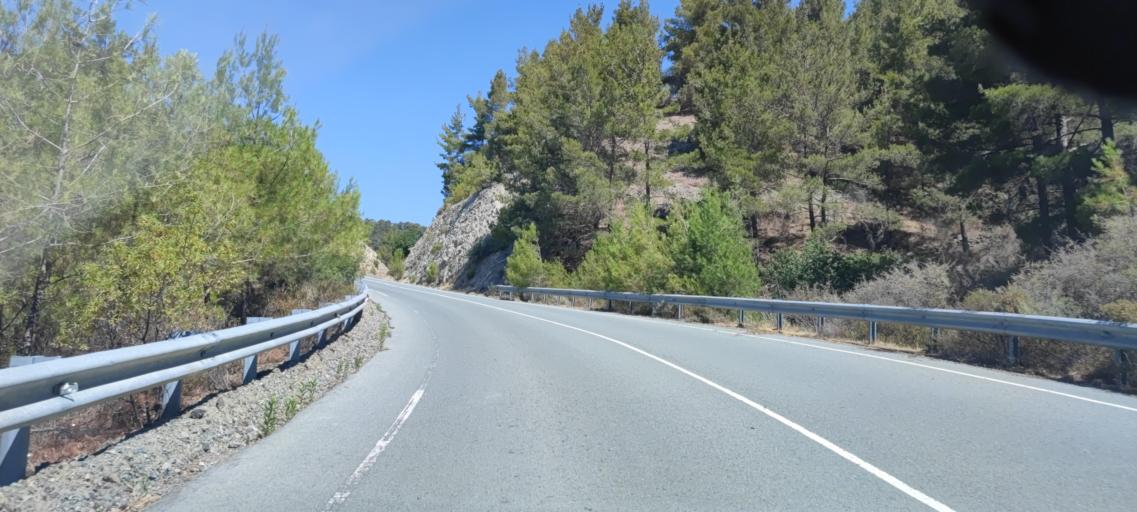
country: CY
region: Limassol
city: Pachna
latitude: 34.9000
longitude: 32.8159
